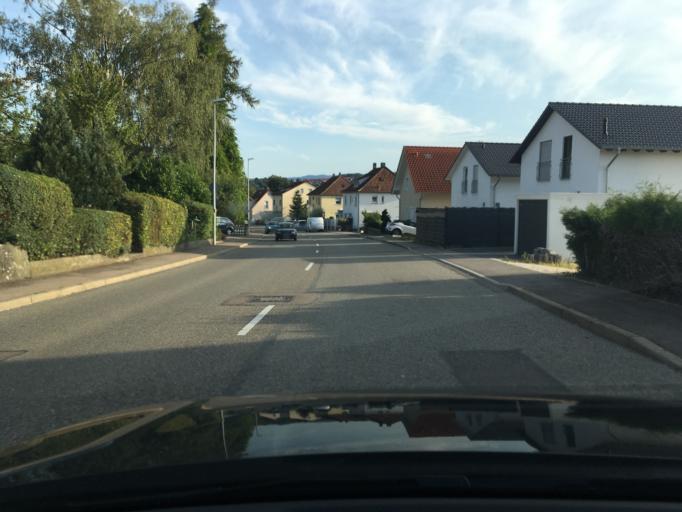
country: DE
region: Baden-Wuerttemberg
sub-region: Regierungsbezirk Stuttgart
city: Uhingen
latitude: 48.7121
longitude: 9.5799
